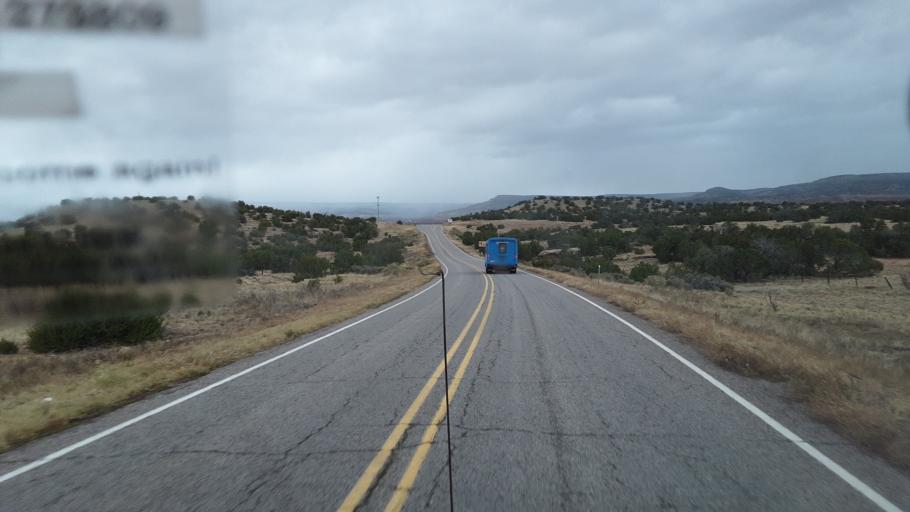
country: US
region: New Mexico
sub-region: Rio Arriba County
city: Santa Teresa
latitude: 36.2507
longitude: -106.4065
